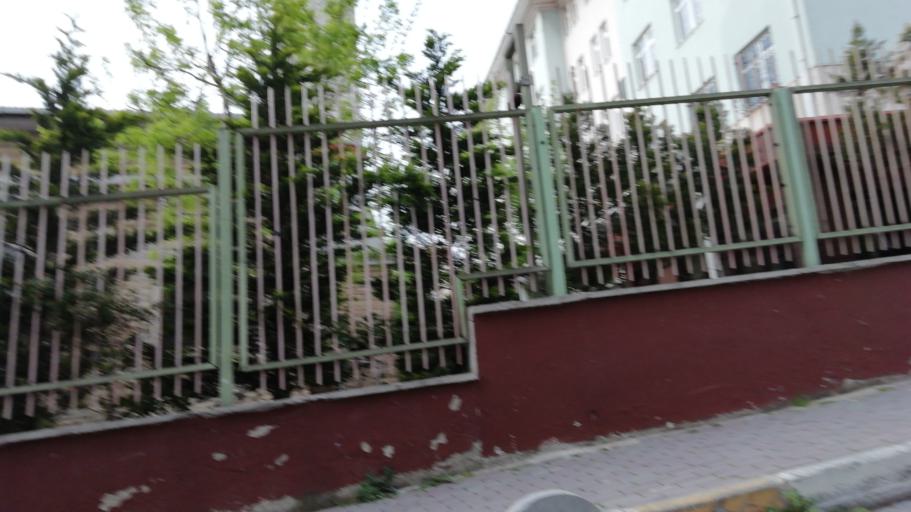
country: TR
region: Istanbul
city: Bagcilar
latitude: 41.0237
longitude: 28.8341
